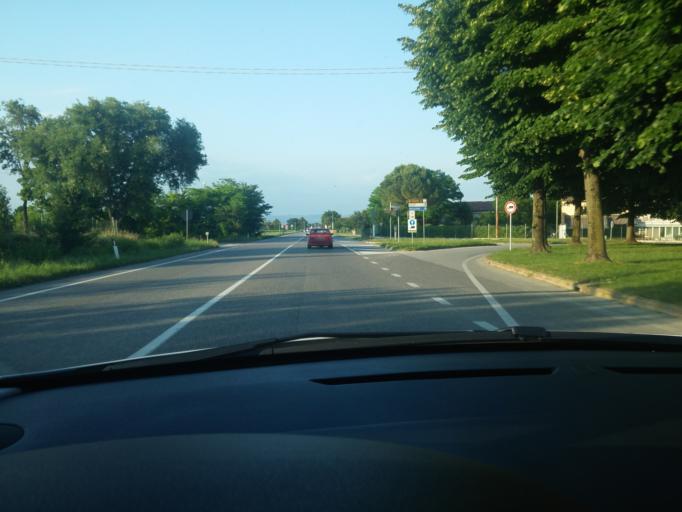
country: IT
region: Friuli Venezia Giulia
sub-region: Provincia di Gorizia
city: Villesse
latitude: 45.8602
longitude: 13.4324
